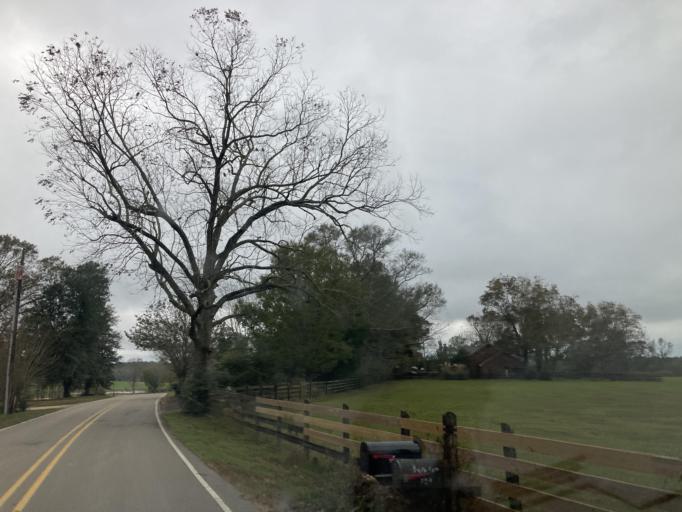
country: US
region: Mississippi
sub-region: Lamar County
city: Purvis
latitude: 31.1822
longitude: -89.4567
